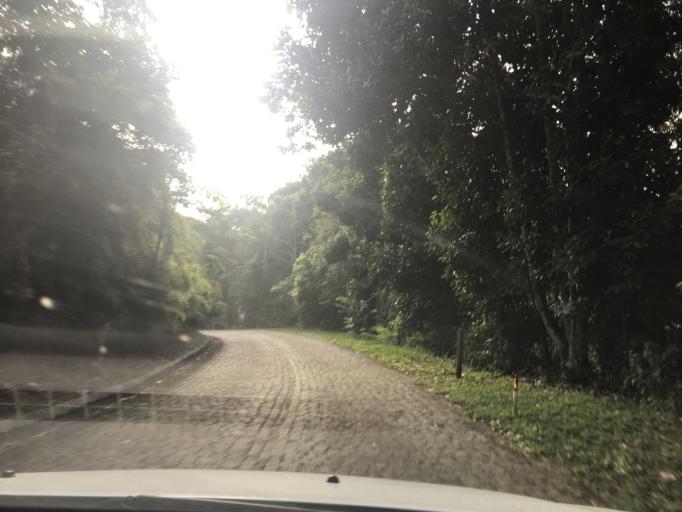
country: BR
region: Bahia
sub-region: Gandu
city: Gandu
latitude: -13.9004
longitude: -39.4706
